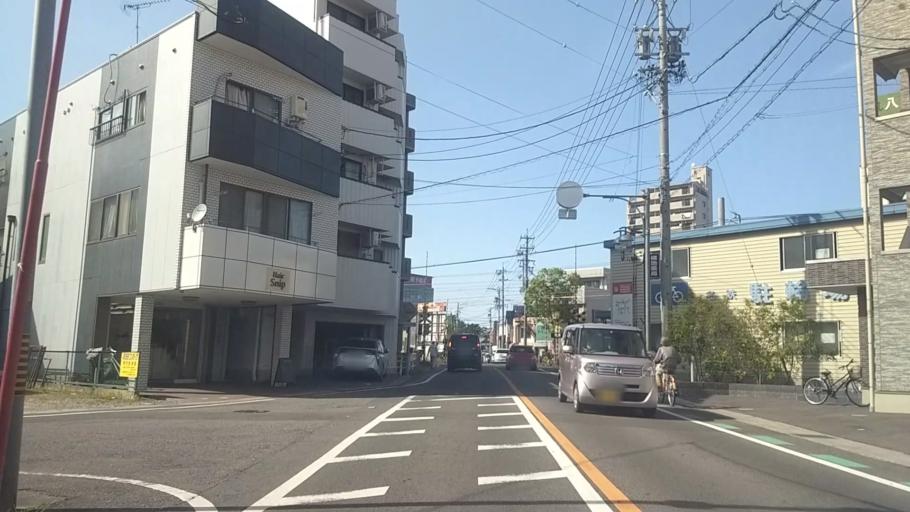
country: JP
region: Aichi
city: Anjo
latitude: 34.9872
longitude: 137.0839
